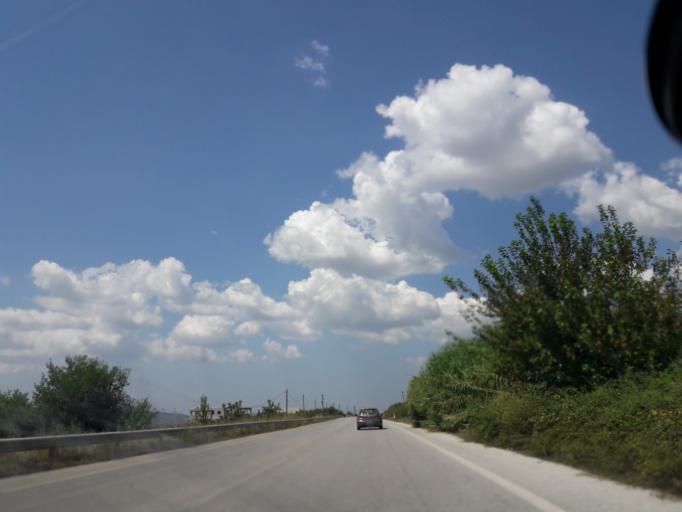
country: GR
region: Central Macedonia
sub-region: Nomos Chalkidikis
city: Galatista
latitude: 40.4626
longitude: 23.2749
